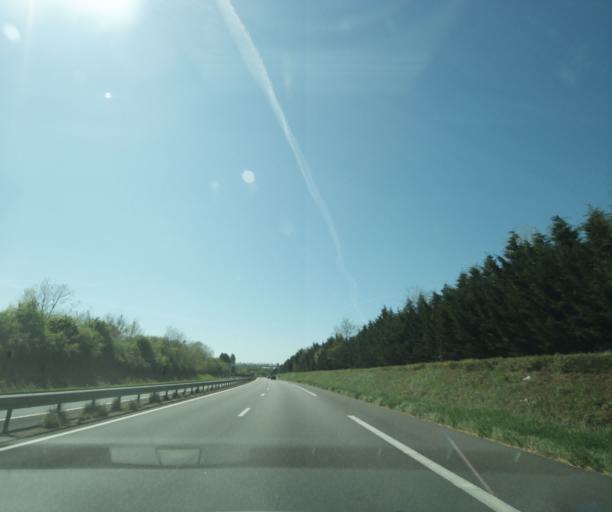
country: FR
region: Centre
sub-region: Departement de l'Indre
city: Luant
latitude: 46.7386
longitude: 1.6130
